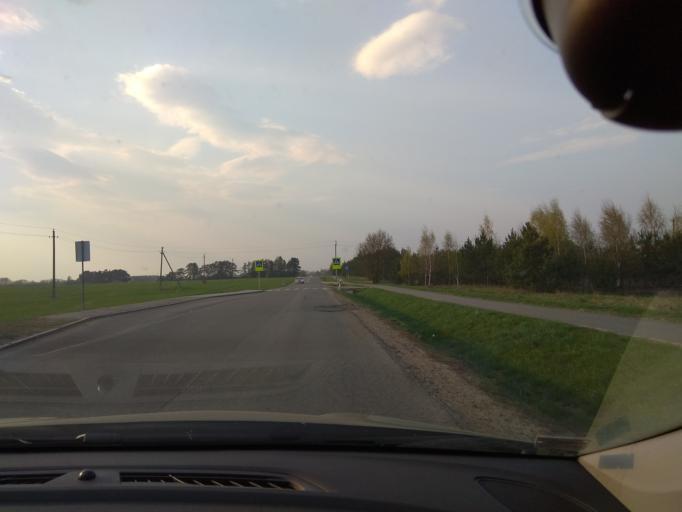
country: LT
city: Grigiskes
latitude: 54.6167
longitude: 25.1171
